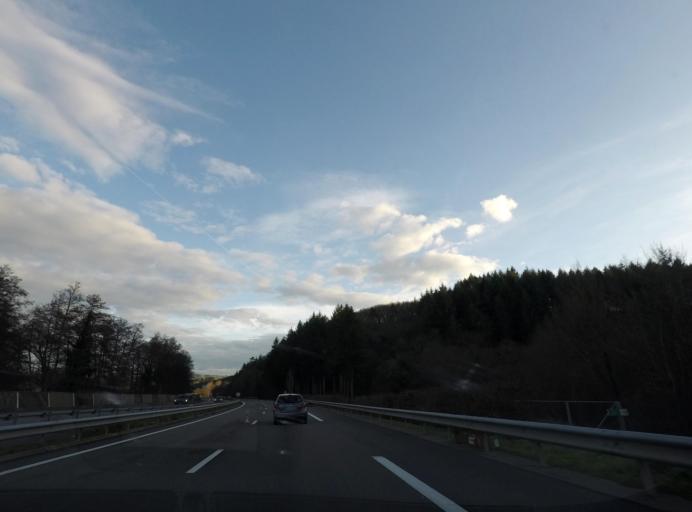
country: FR
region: Bourgogne
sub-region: Departement de Saone-et-Loire
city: Matour
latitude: 46.3768
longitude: 4.5306
